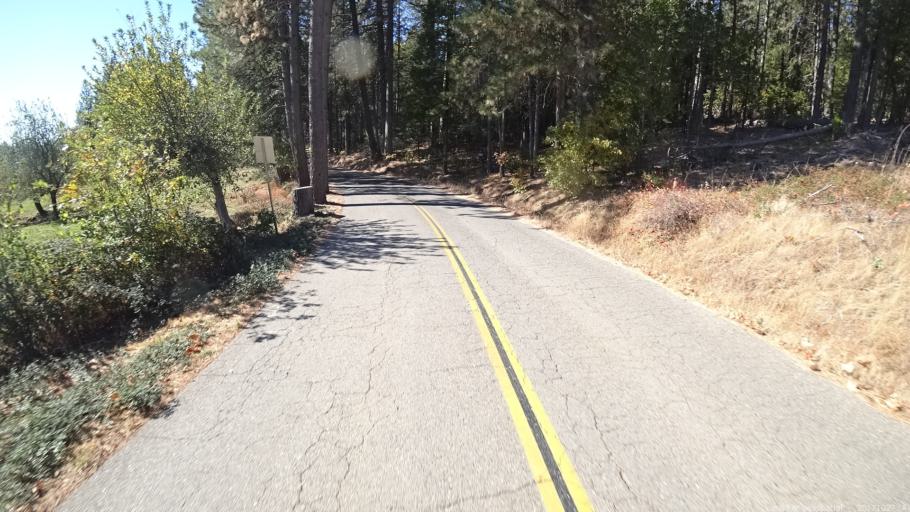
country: US
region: California
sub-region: Shasta County
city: Shingletown
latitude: 40.7183
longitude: -121.9420
